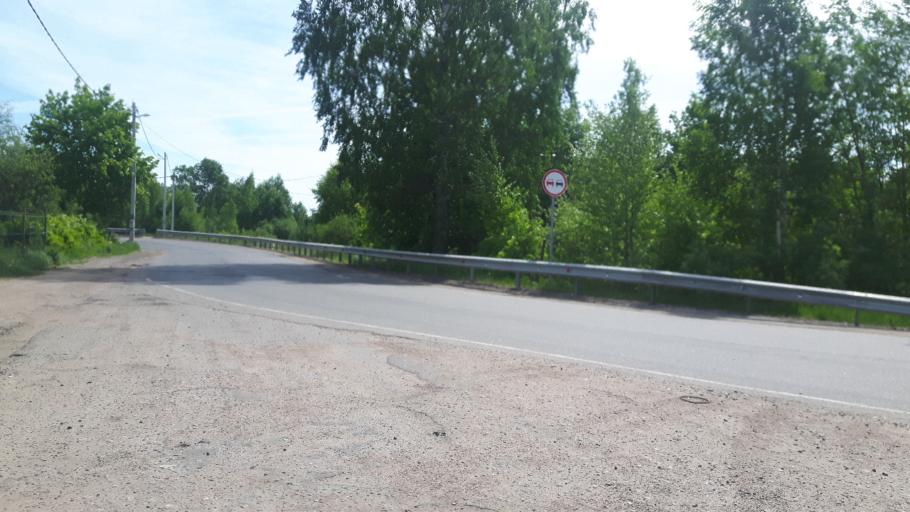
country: RU
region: Leningrad
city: Ust'-Luga
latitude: 59.6567
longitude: 28.2540
